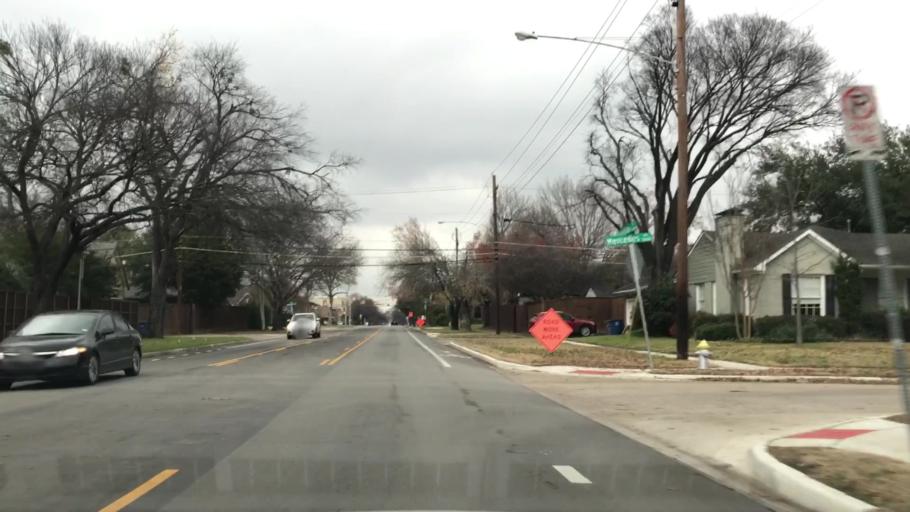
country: US
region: Texas
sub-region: Dallas County
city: Highland Park
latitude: 32.8279
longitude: -96.7680
